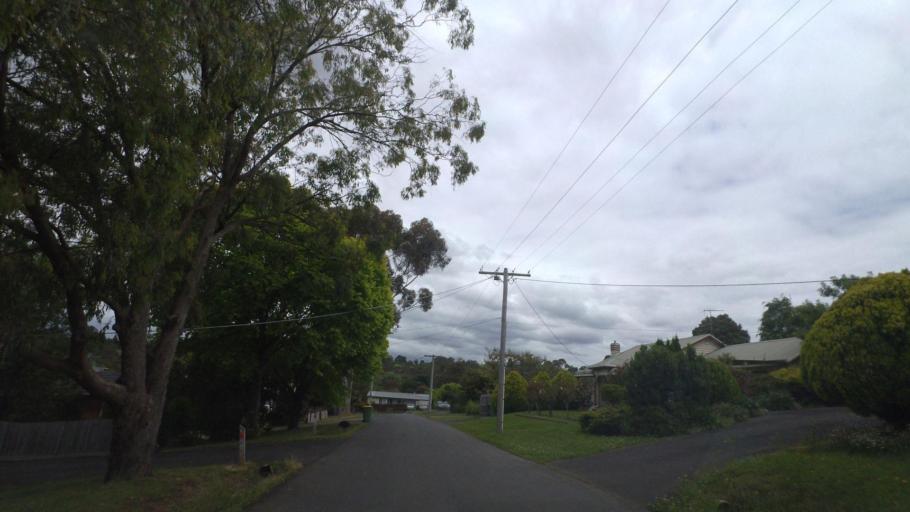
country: AU
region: Victoria
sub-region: Yarra Ranges
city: Mount Evelyn
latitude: -37.7844
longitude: 145.4295
